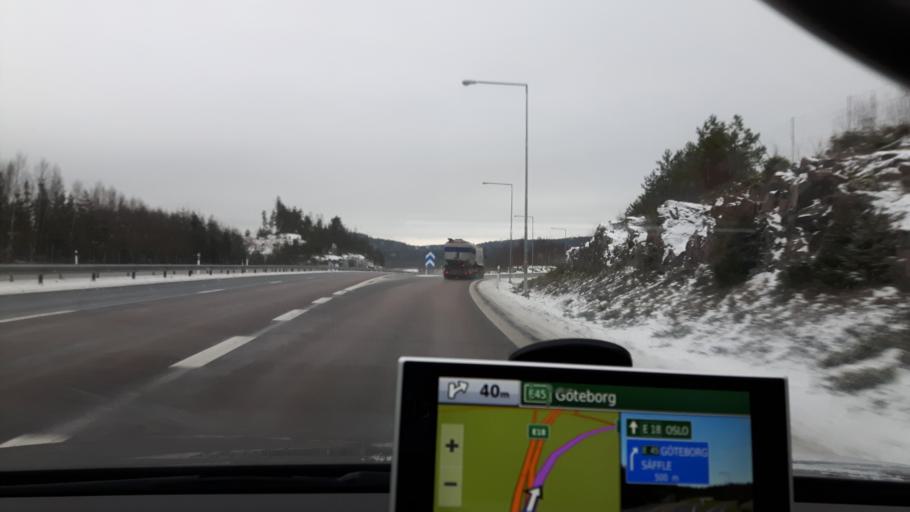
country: SE
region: Vaermland
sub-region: Grums Kommun
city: Slottsbron
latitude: 59.2665
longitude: 13.0081
